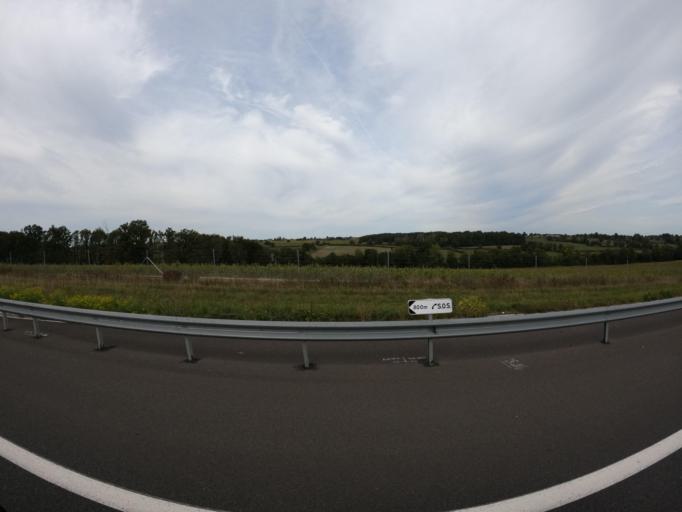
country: FR
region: Auvergne
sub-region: Departement de l'Allier
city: Bessay-sur-Allier
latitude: 46.4686
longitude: 3.2951
